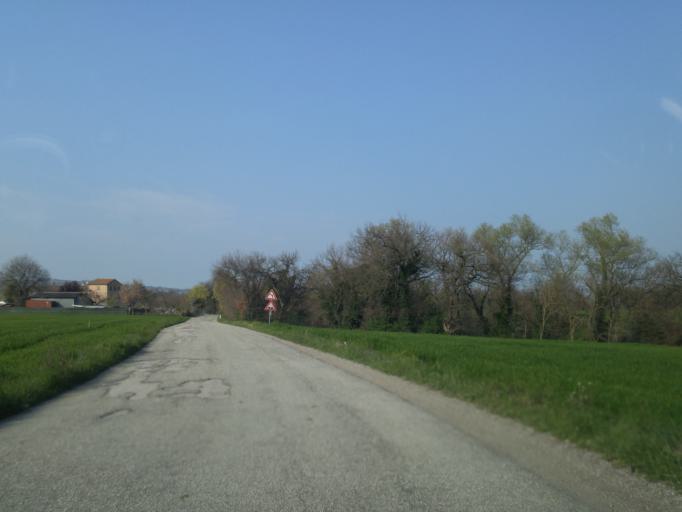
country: IT
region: The Marches
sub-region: Provincia di Pesaro e Urbino
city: Tavernelle
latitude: 43.7059
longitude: 12.8870
